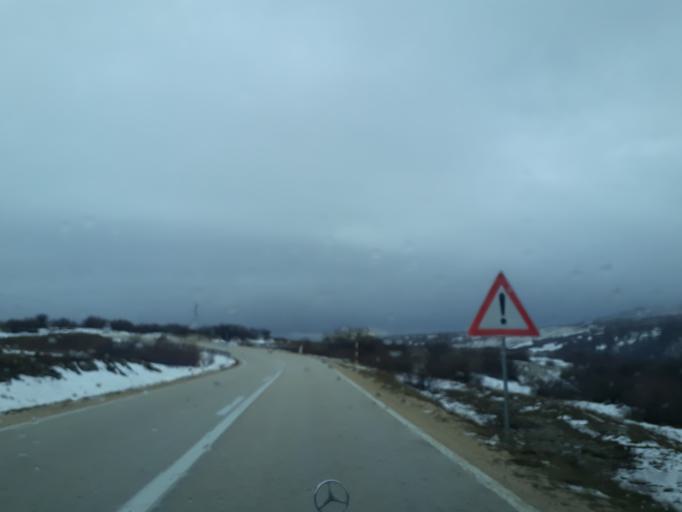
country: BA
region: Federation of Bosnia and Herzegovina
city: Tomislavgrad
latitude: 43.7997
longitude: 17.2095
